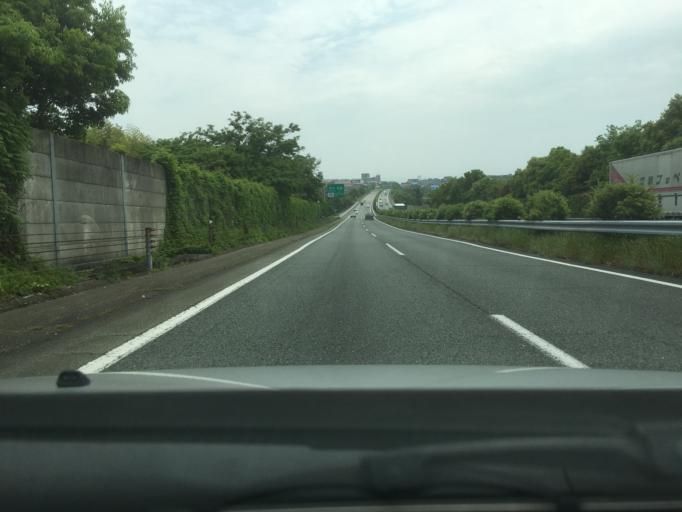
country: JP
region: Kumamoto
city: Kumamoto
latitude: 32.8456
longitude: 130.7708
